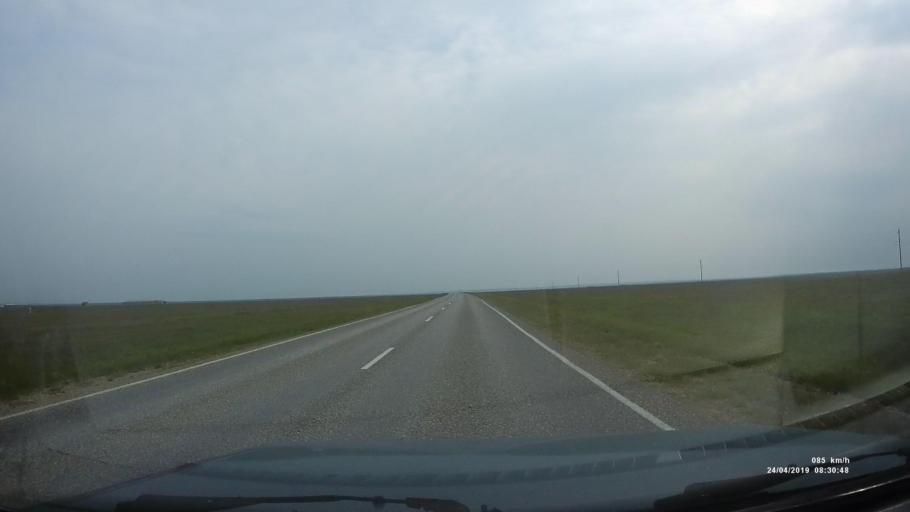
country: RU
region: Kalmykiya
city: Priyutnoye
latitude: 46.1622
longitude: 43.8510
